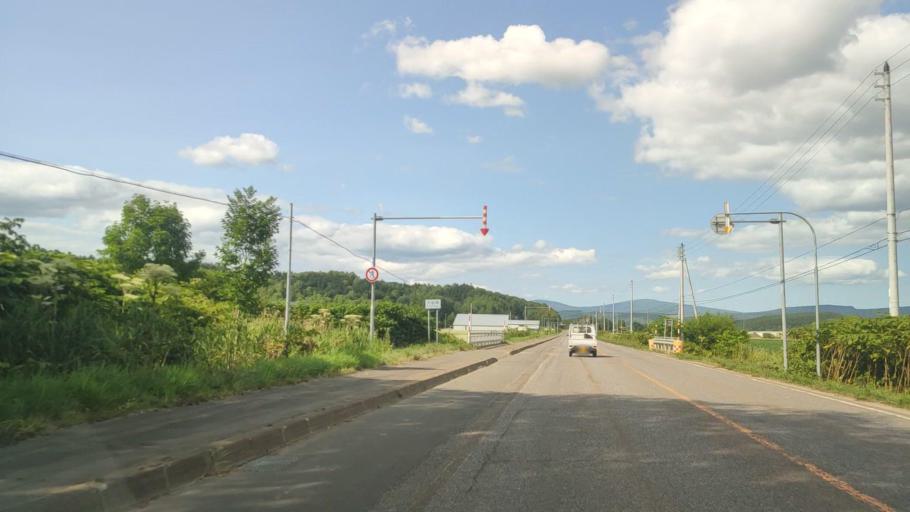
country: JP
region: Hokkaido
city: Nayoro
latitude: 44.3985
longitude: 142.3952
